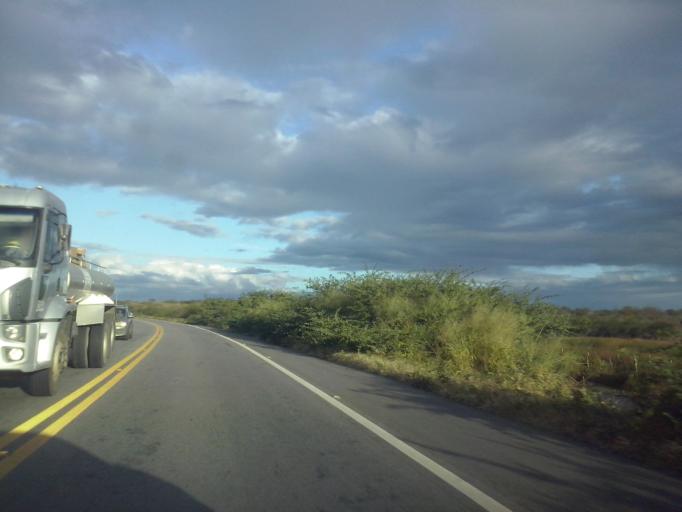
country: BR
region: Paraiba
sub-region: Patos
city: Patos
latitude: -6.9464
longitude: -37.4030
